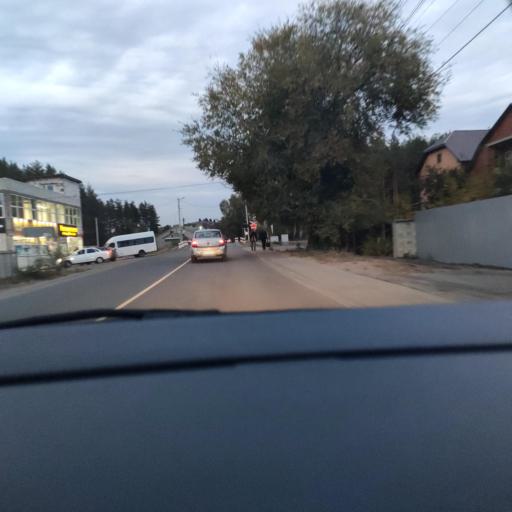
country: RU
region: Voronezj
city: Podgornoye
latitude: 51.7403
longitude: 39.1660
